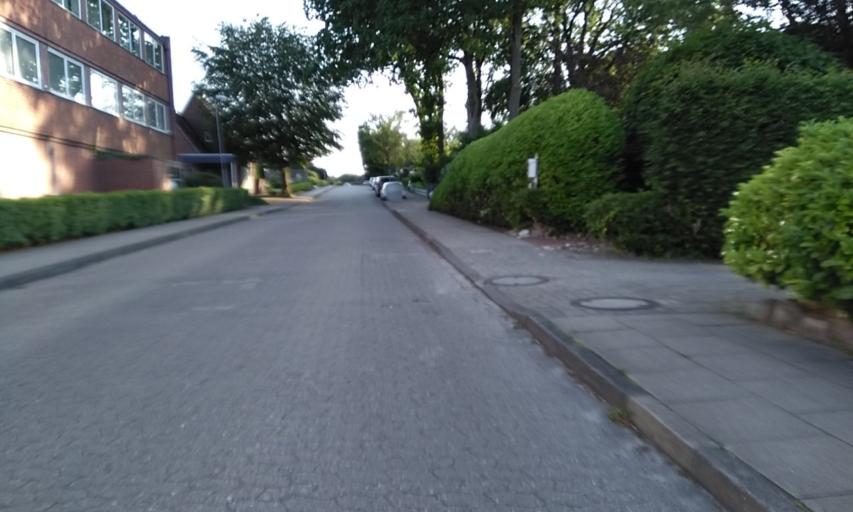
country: DE
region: Lower Saxony
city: Dollern
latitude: 53.5416
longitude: 9.5548
